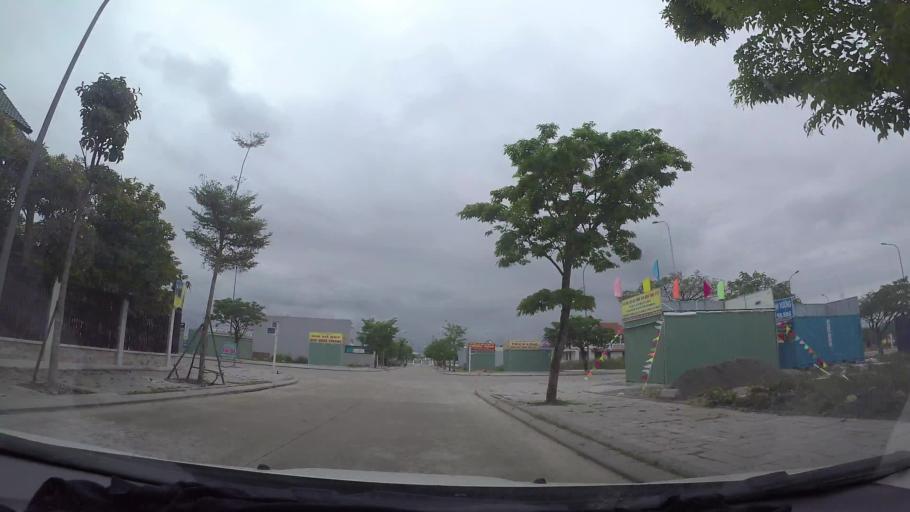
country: VN
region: Da Nang
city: Lien Chieu
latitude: 16.1043
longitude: 108.1190
